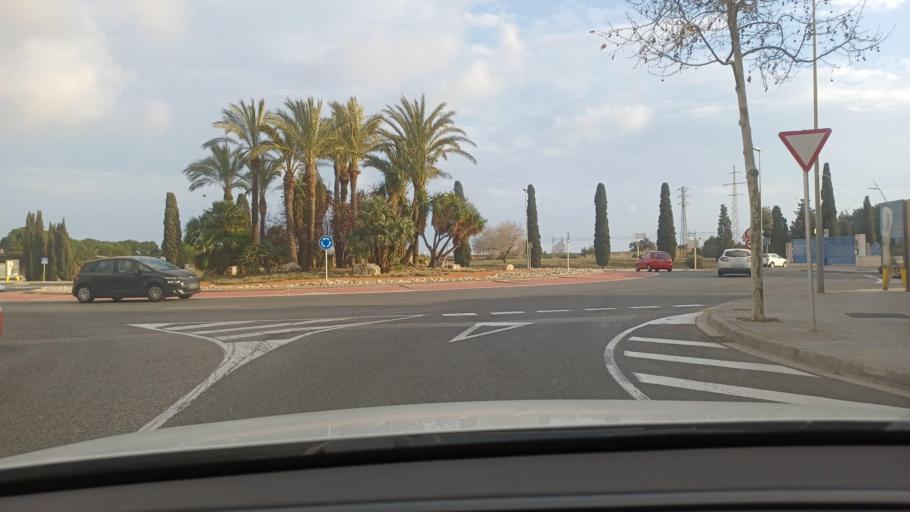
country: ES
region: Catalonia
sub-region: Provincia de Tarragona
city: Vila-seca
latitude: 41.1139
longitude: 1.1554
